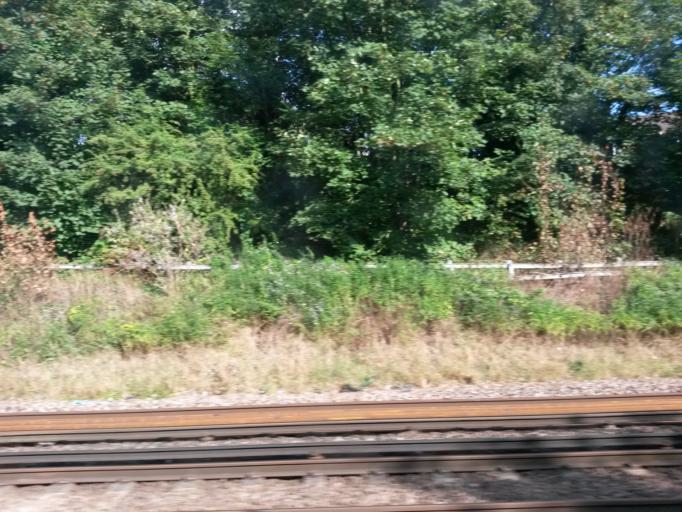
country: GB
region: England
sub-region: Greater London
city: Thornton Heath
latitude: 51.4112
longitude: -0.0666
